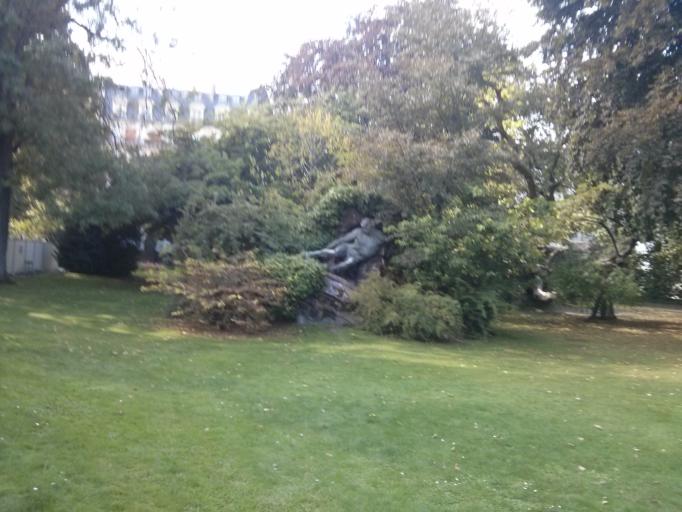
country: FR
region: Ile-de-France
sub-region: Paris
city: Paris
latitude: 48.8484
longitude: 2.3338
